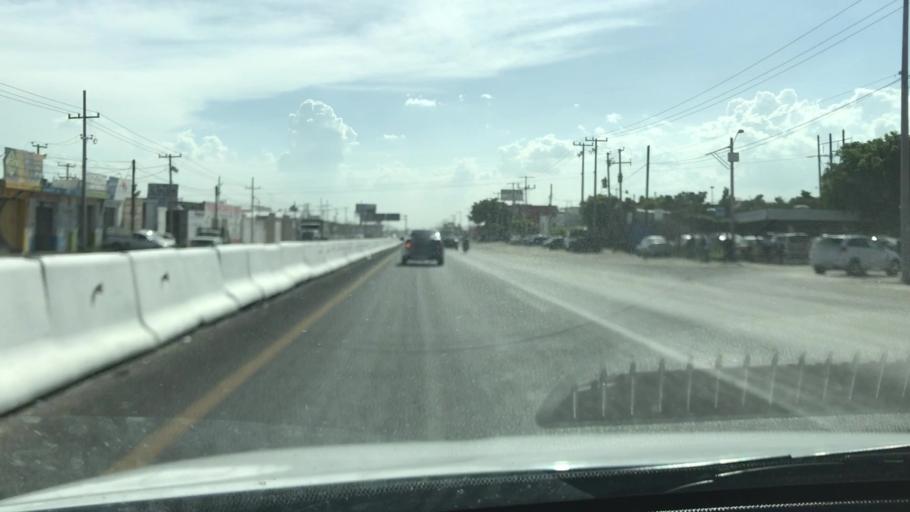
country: MX
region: Guanajuato
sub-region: Celaya
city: Colonia Pedro Maria Anaya
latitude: 20.5182
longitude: -100.8550
